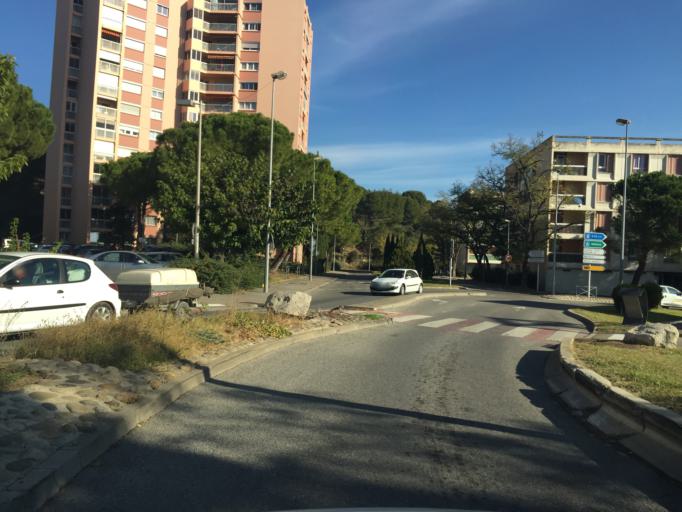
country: FR
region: Provence-Alpes-Cote d'Azur
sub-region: Departement des Bouches-du-Rhone
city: Salon-de-Provence
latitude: 43.6534
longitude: 5.0990
